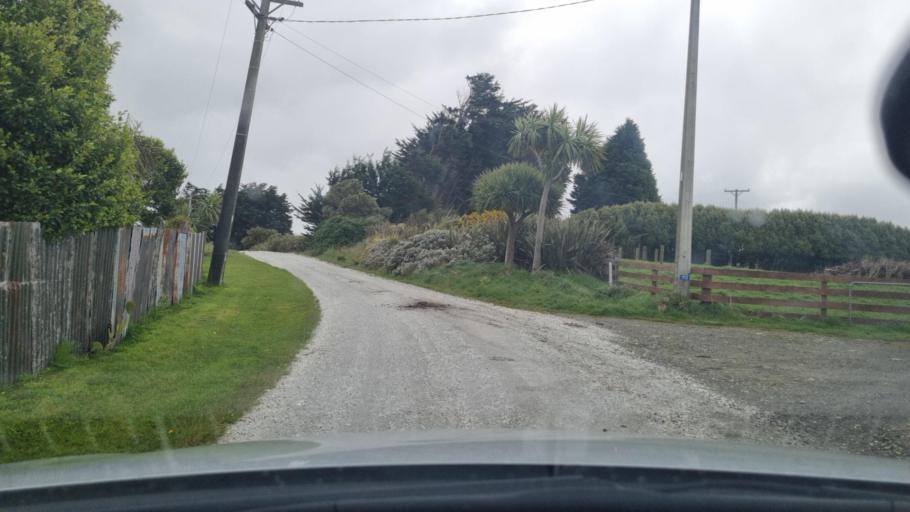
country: NZ
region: Southland
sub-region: Invercargill City
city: Bluff
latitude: -46.5389
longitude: 168.2904
